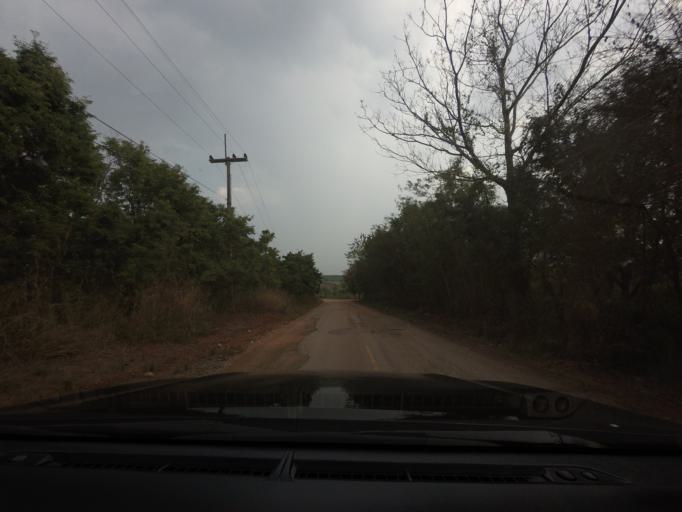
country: TH
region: Nakhon Ratchasima
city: Wang Nam Khiao
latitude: 14.4383
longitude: 101.6951
